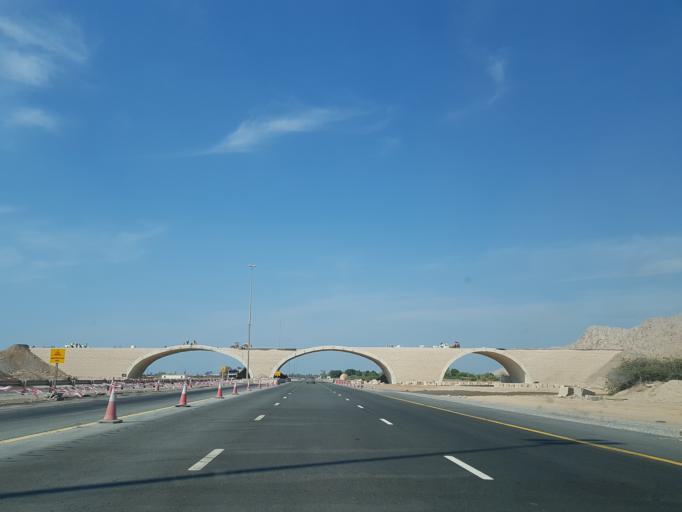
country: AE
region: Ra's al Khaymah
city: Ras al-Khaimah
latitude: 25.8193
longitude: 56.0253
